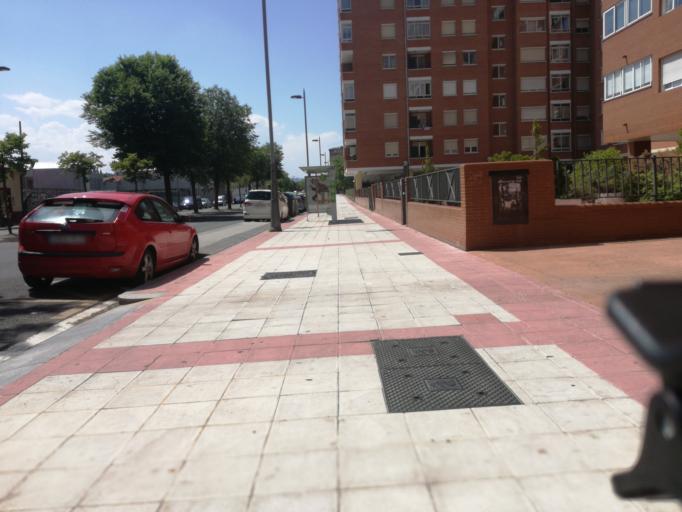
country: ES
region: Basque Country
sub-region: Provincia de Alava
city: Gasteiz / Vitoria
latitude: 42.8538
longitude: -2.6991
